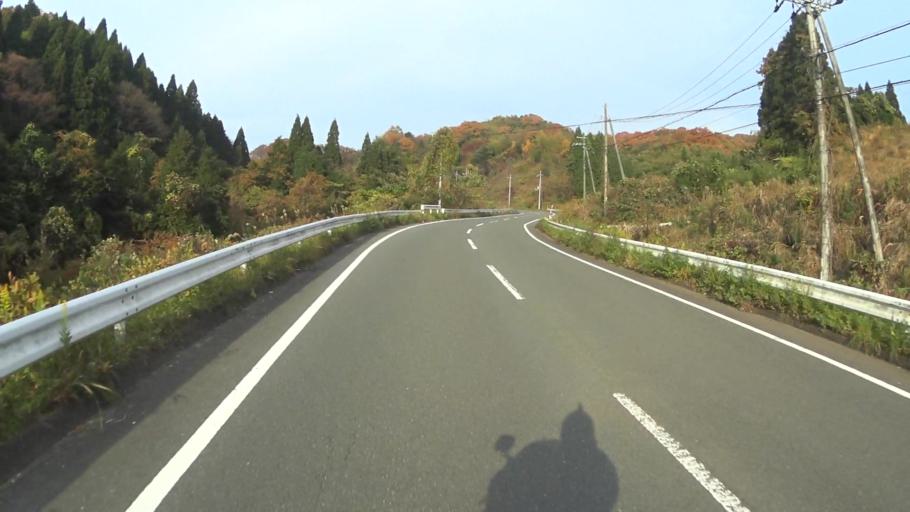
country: JP
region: Kyoto
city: Maizuru
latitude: 35.5114
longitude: 135.4563
